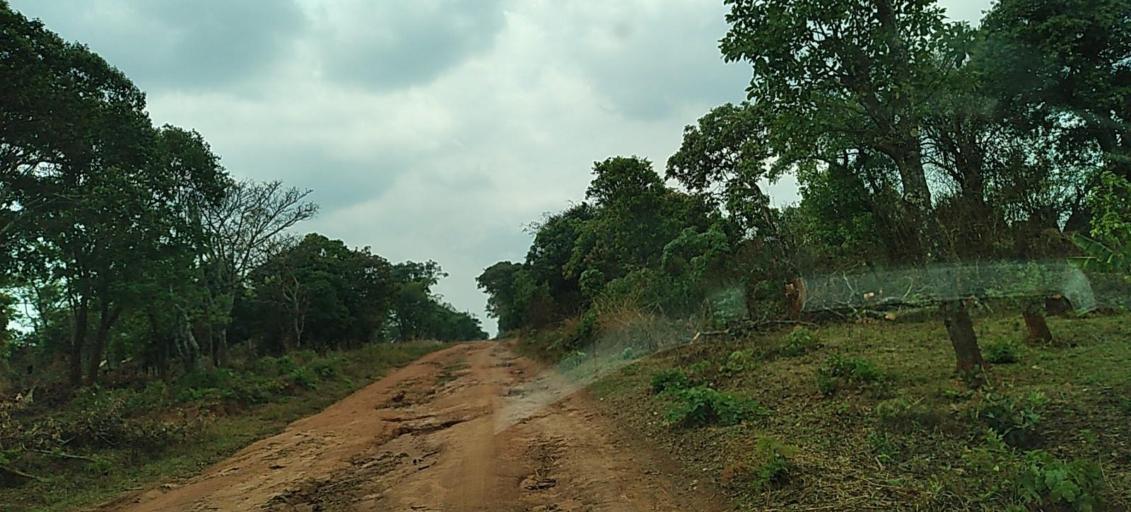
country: ZM
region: North-Western
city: Mwinilunga
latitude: -11.5337
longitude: 24.7840
